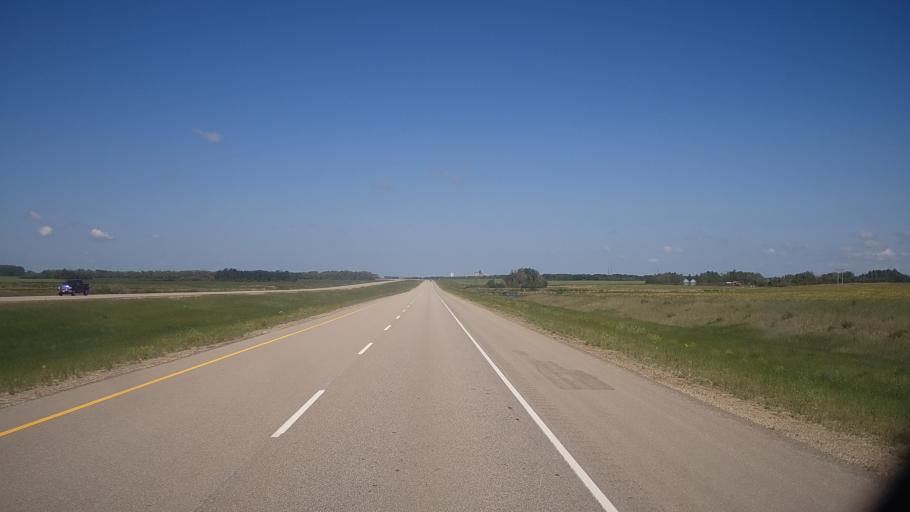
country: CA
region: Saskatchewan
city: Saskatoon
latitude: 52.0050
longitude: -106.3427
